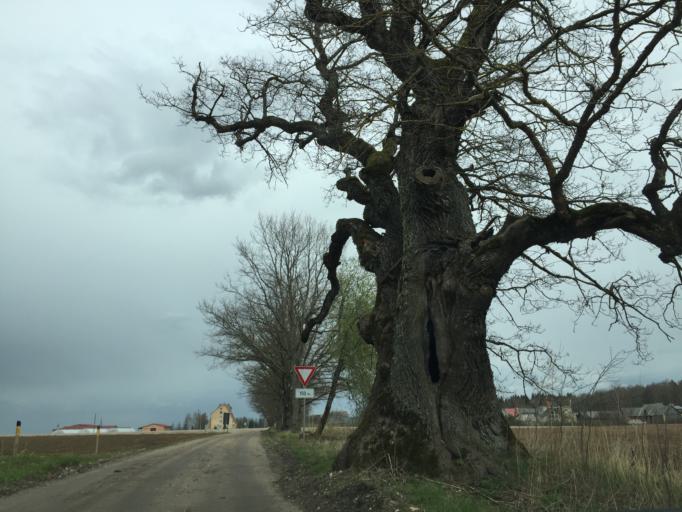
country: LV
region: Priekuli
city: Priekuli
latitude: 57.3090
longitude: 25.3395
